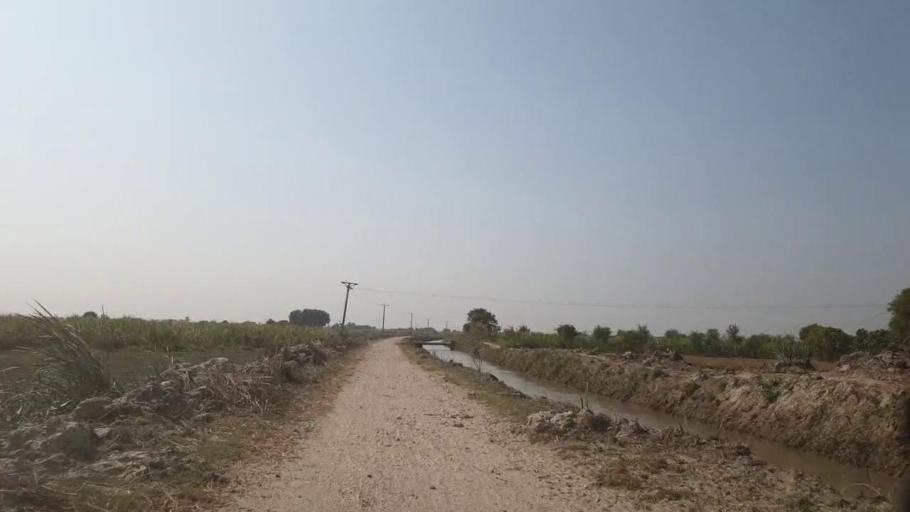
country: PK
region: Sindh
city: Bulri
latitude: 24.9531
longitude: 68.3812
